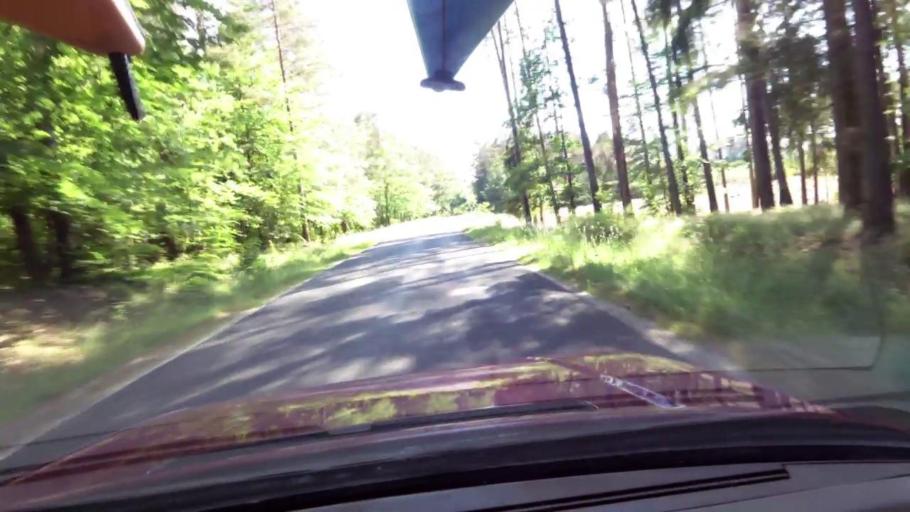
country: PL
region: Pomeranian Voivodeship
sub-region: Powiat slupski
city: Kepice
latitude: 54.2052
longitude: 16.8901
